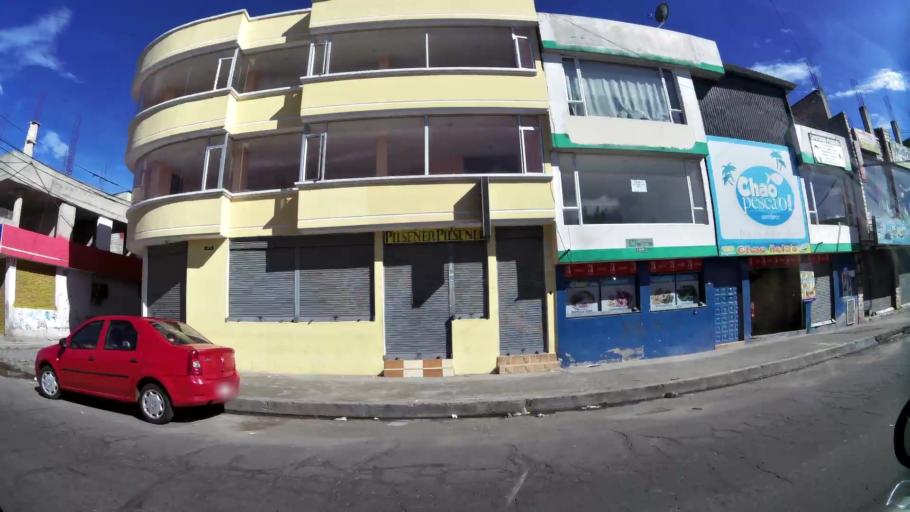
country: EC
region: Pichincha
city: Quito
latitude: -0.2979
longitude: -78.5649
